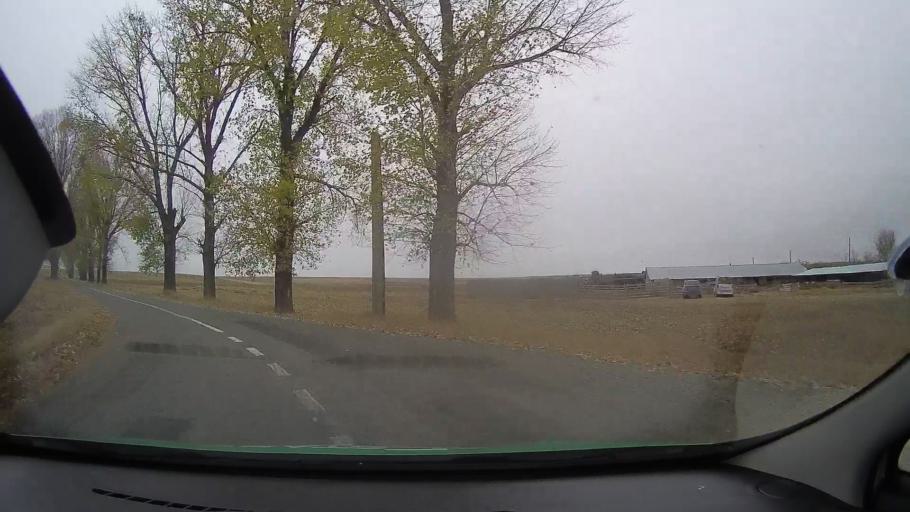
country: RO
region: Constanta
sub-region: Comuna Saraiu
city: Saraiu
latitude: 44.7266
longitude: 28.2204
